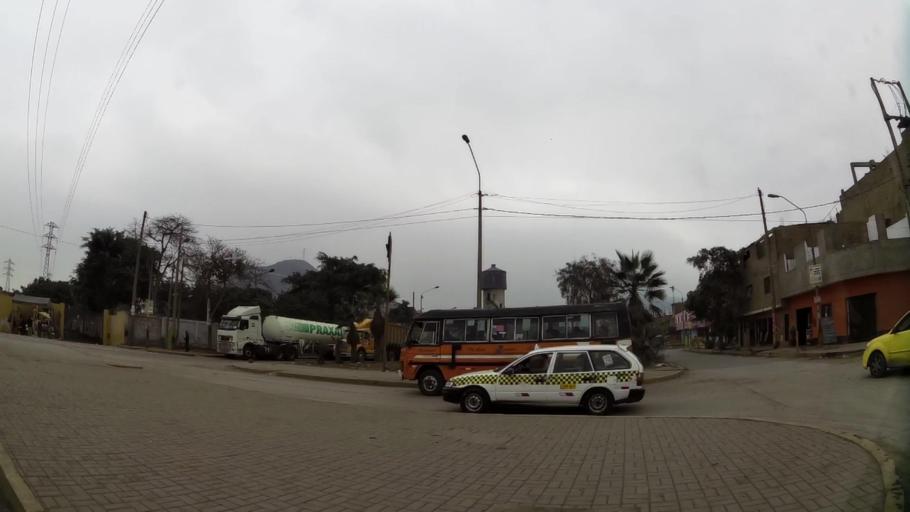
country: PE
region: Lima
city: Lima
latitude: -12.0363
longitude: -77.0069
